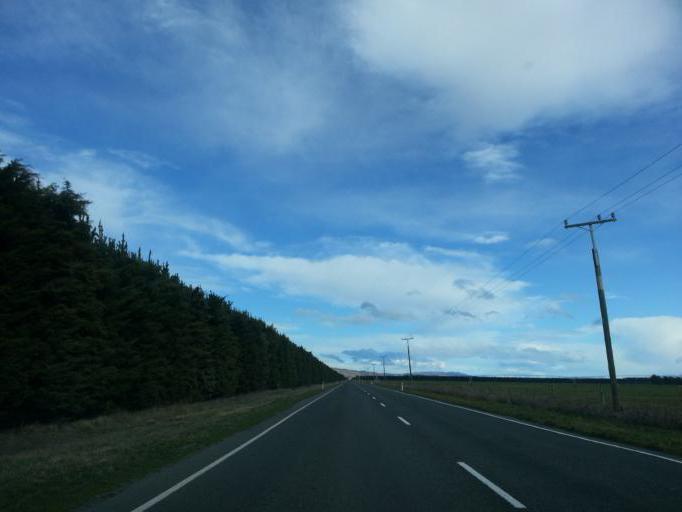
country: NZ
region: Canterbury
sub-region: Hurunui District
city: Amberley
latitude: -42.8032
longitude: 172.8248
